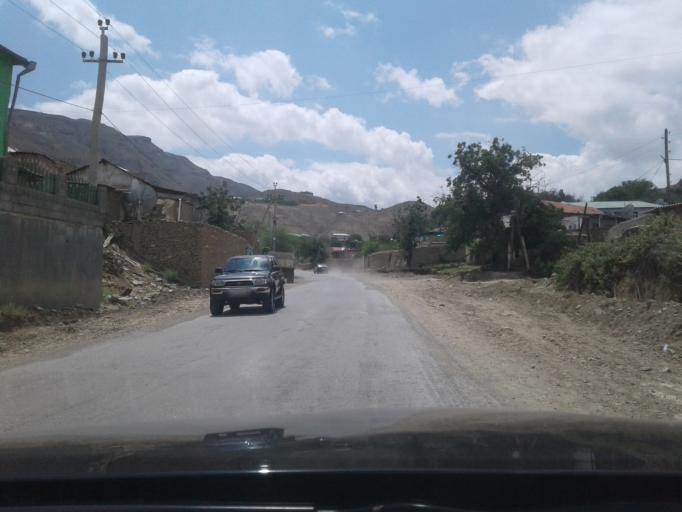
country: TM
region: Ahal
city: Baharly
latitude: 38.4731
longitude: 57.0336
